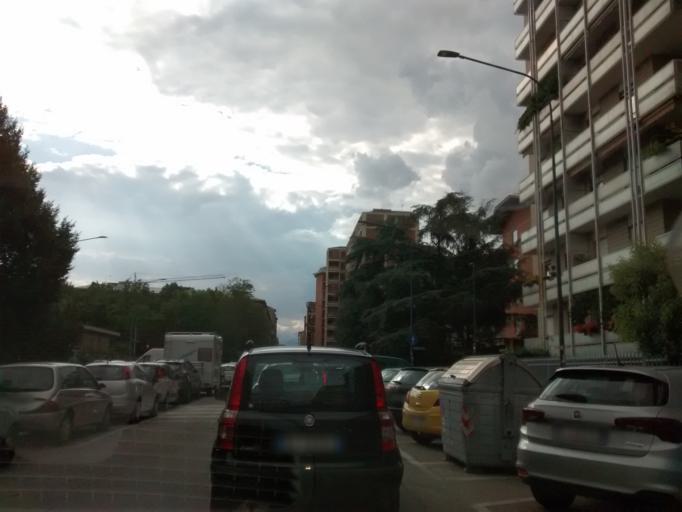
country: IT
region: Piedmont
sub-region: Provincia di Torino
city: Lesna
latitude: 45.0402
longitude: 7.6423
